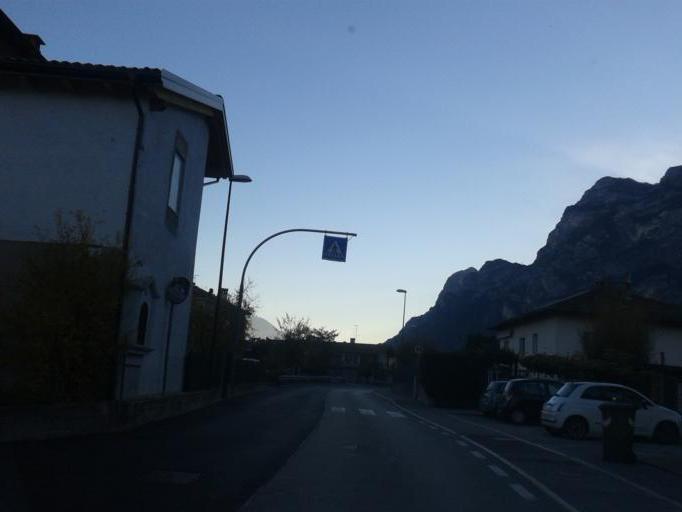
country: IT
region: Trentino-Alto Adige
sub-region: Provincia di Trento
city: Riva del Garda
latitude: 45.9053
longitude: 10.8515
